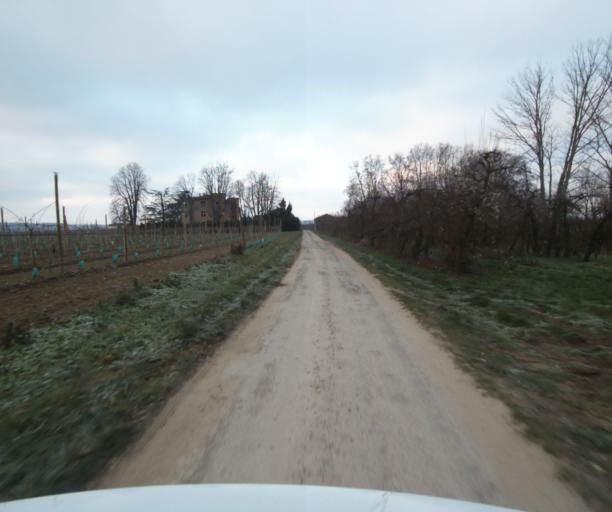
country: FR
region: Midi-Pyrenees
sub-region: Departement du Tarn-et-Garonne
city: Moissac
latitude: 44.0952
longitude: 1.1264
